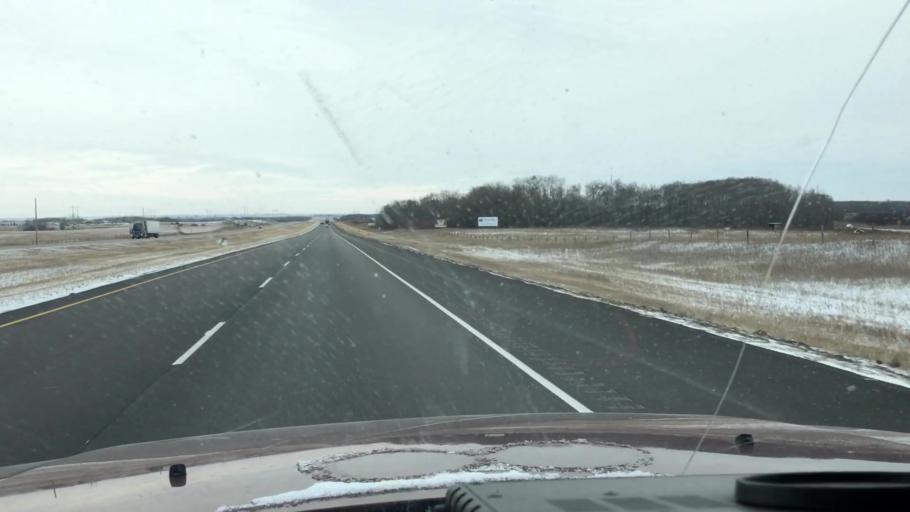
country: CA
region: Saskatchewan
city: Saskatoon
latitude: 51.9028
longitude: -106.5226
